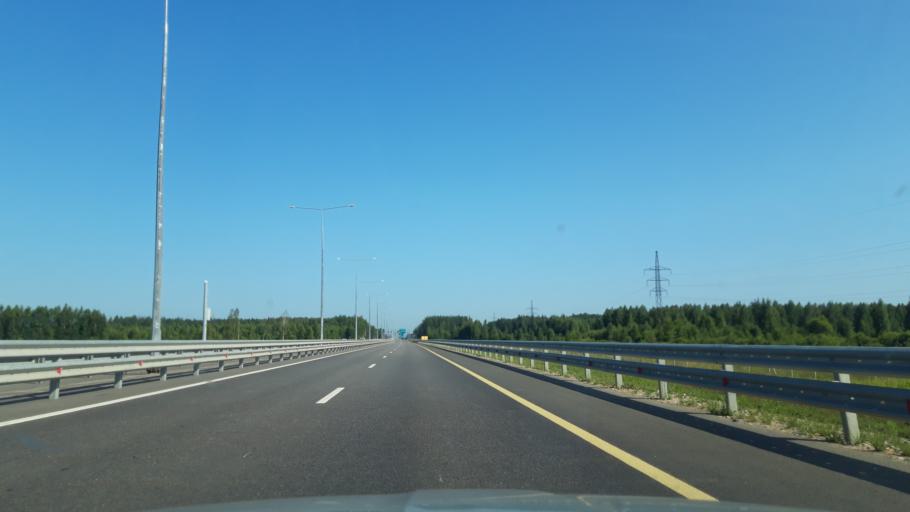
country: RU
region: Tverskaya
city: Zavidovo
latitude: 56.5524
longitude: 36.4878
